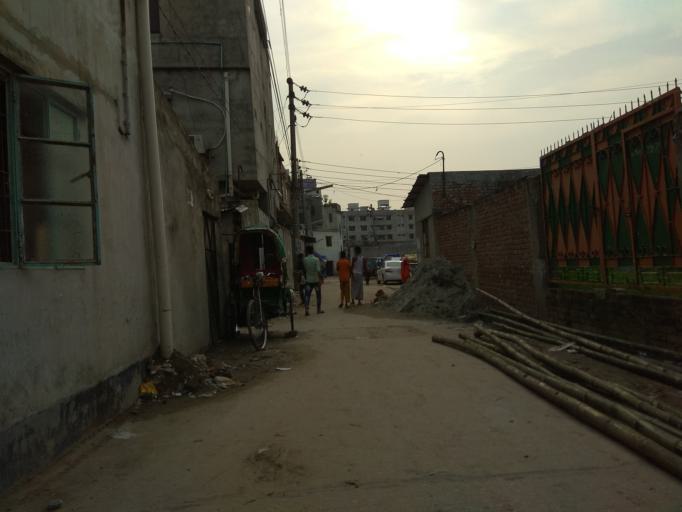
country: BD
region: Dhaka
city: Azimpur
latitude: 23.8113
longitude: 90.3820
